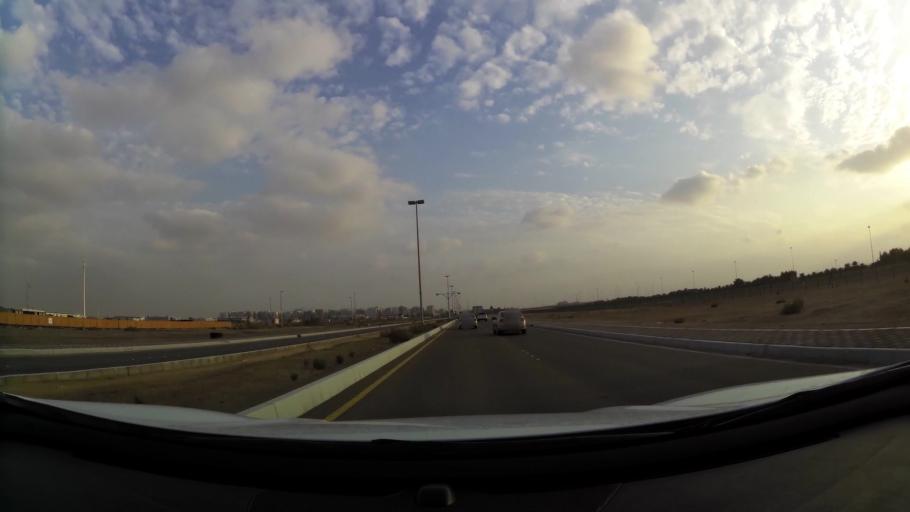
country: AE
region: Abu Dhabi
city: Abu Dhabi
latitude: 24.3571
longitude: 54.5284
